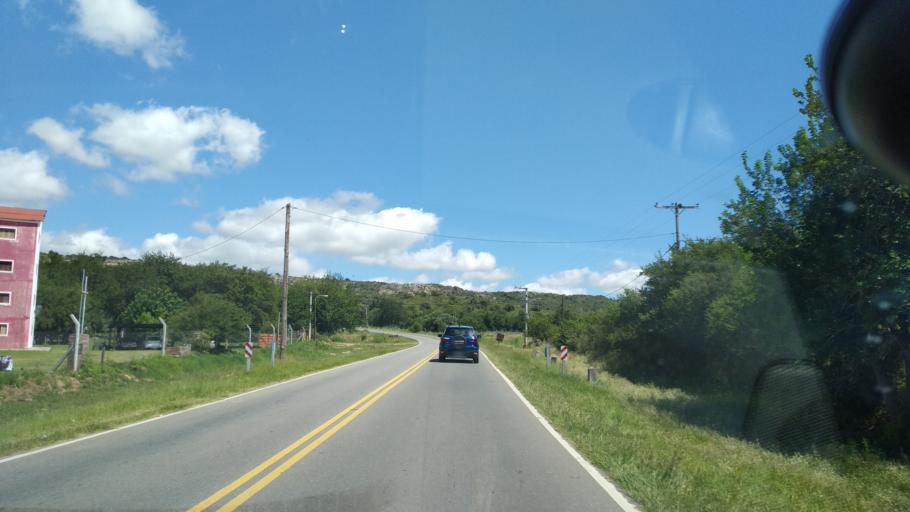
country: AR
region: Cordoba
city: Villa Cura Brochero
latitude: -31.6937
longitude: -65.0439
